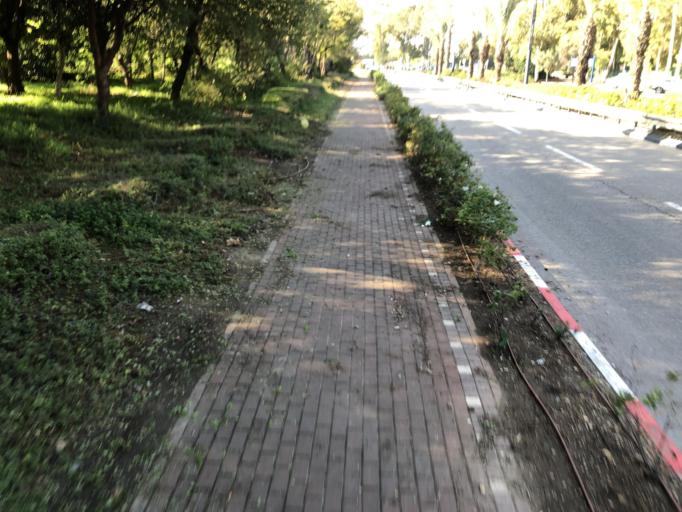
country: IL
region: Northern District
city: `Akko
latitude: 32.9225
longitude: 35.0895
